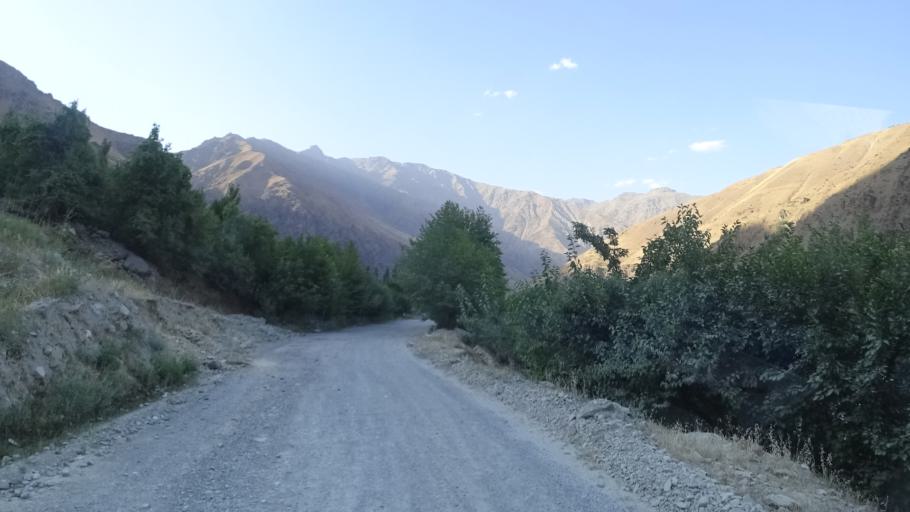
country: TJ
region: Gorno-Badakhshan
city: Qalaikhumb
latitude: 38.3901
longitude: 70.6726
